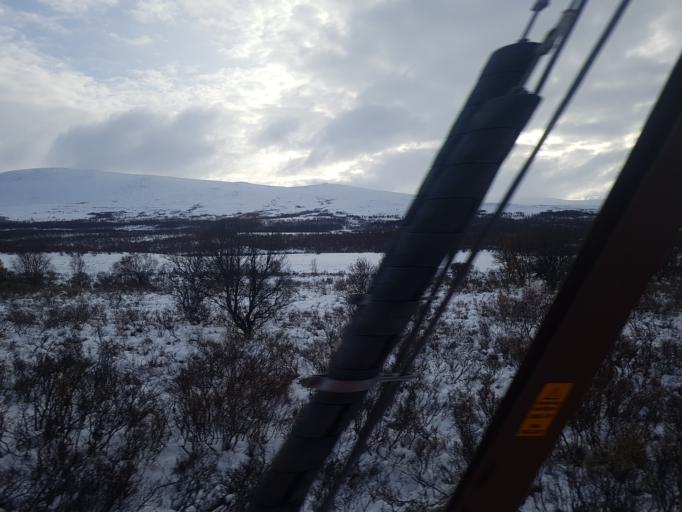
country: NO
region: Oppland
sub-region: Dovre
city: Dovre
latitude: 62.1226
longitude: 9.2981
